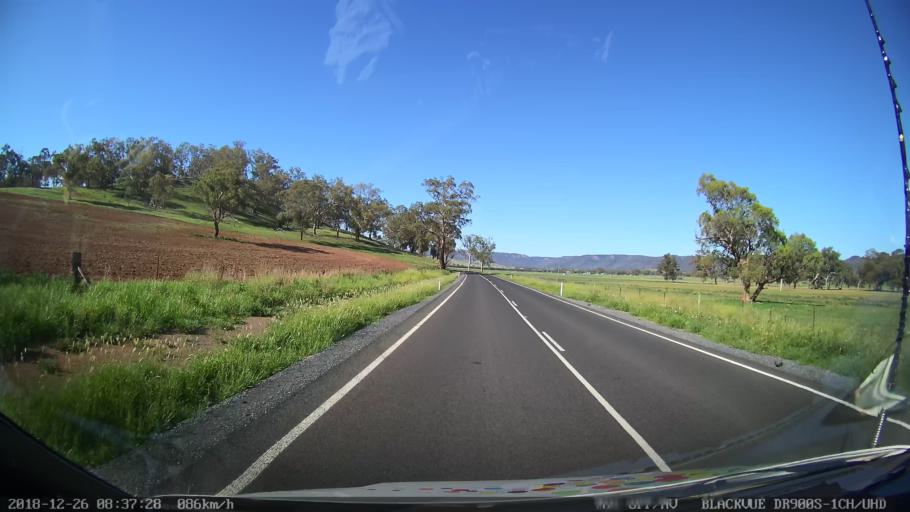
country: AU
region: New South Wales
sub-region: Upper Hunter Shire
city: Merriwa
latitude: -32.4327
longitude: 150.0896
